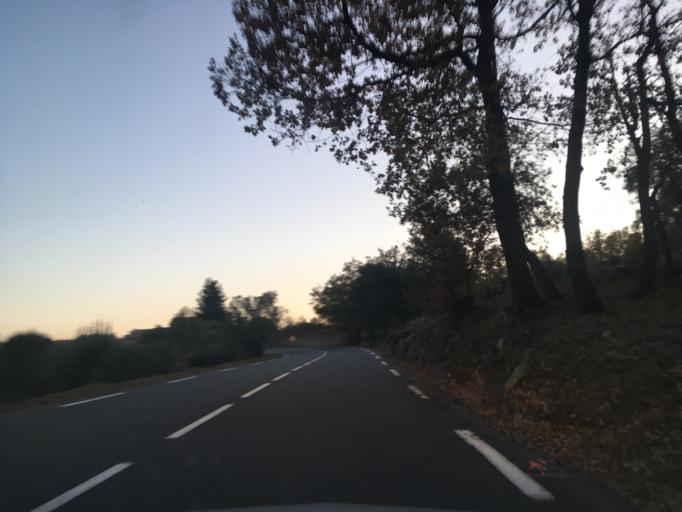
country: FR
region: Provence-Alpes-Cote d'Azur
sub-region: Departement du Var
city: Figanieres
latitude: 43.5481
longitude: 6.5293
